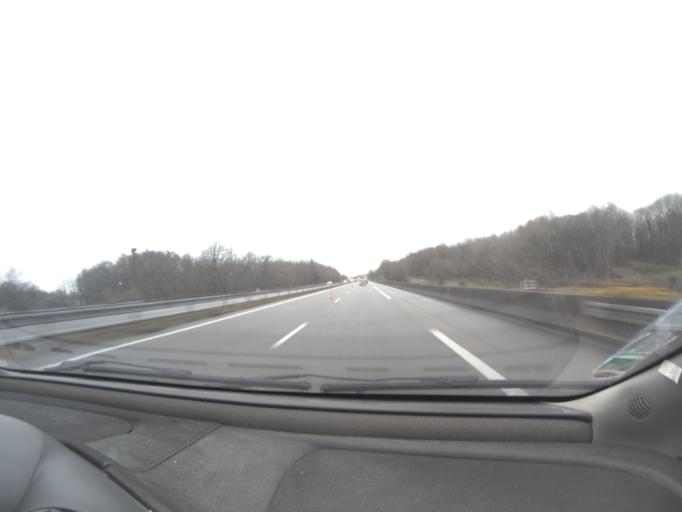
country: FR
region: Pays de la Loire
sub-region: Departement de la Loire-Atlantique
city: Le Cellier
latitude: 47.3525
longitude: -1.3446
